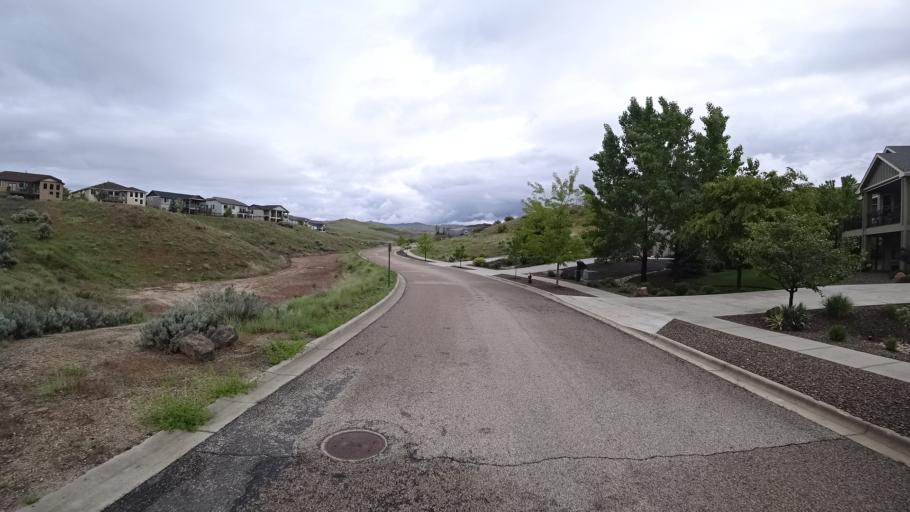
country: US
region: Idaho
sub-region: Ada County
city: Eagle
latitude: 43.7698
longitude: -116.2581
